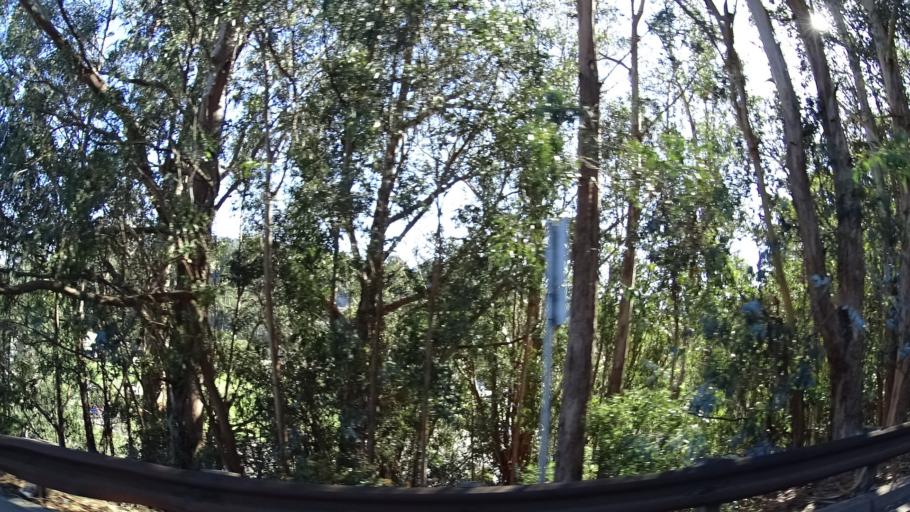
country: US
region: California
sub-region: San Mateo County
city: San Bruno
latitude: 37.6296
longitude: -122.4371
